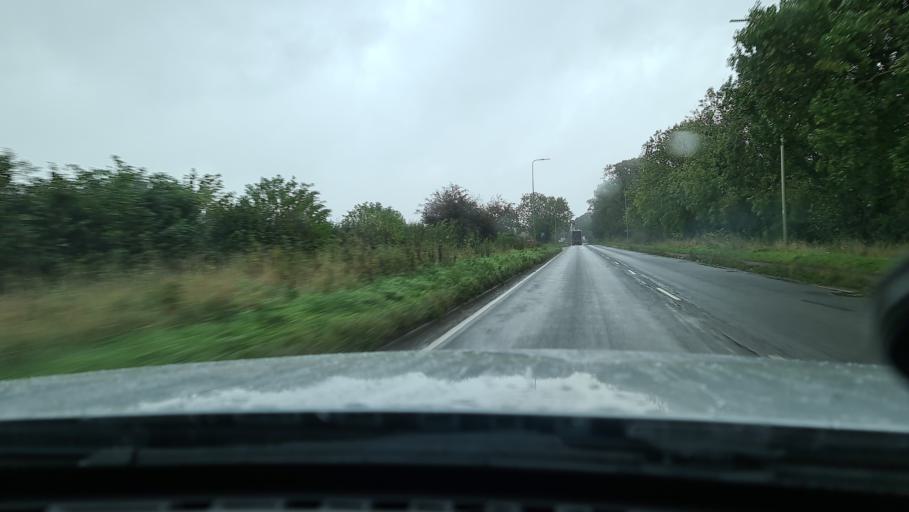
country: GB
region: England
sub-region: Oxfordshire
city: Adderbury
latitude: 52.0303
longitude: -1.3147
